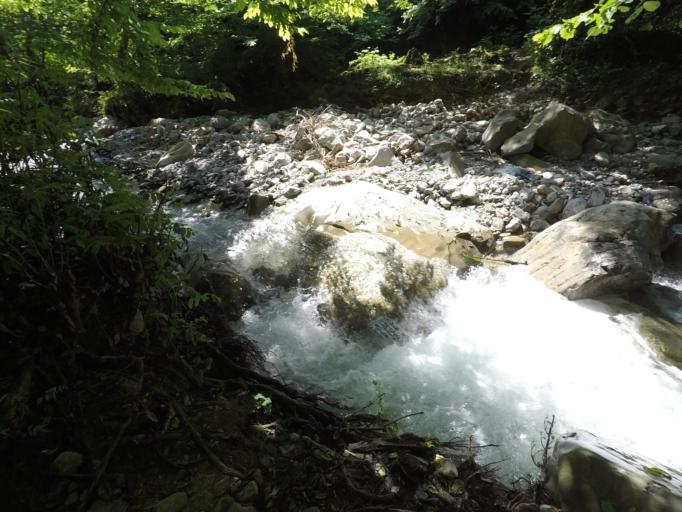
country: AZ
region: Qakh Rayon
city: Cinarli
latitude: 41.4892
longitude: 46.8563
